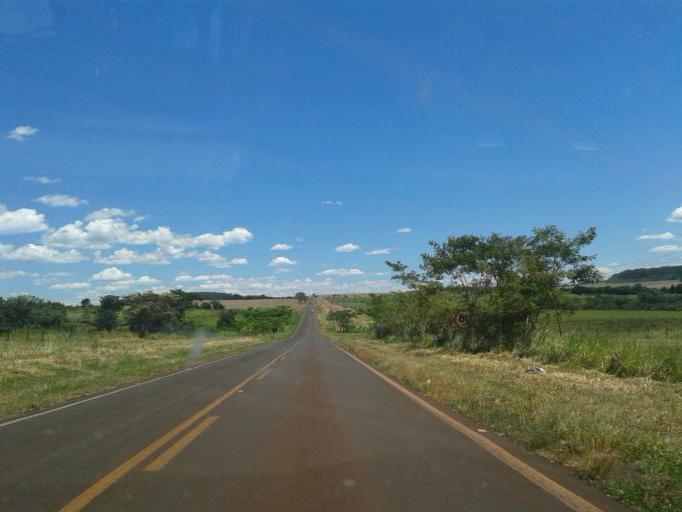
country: BR
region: Minas Gerais
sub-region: Capinopolis
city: Capinopolis
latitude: -18.6222
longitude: -49.5345
